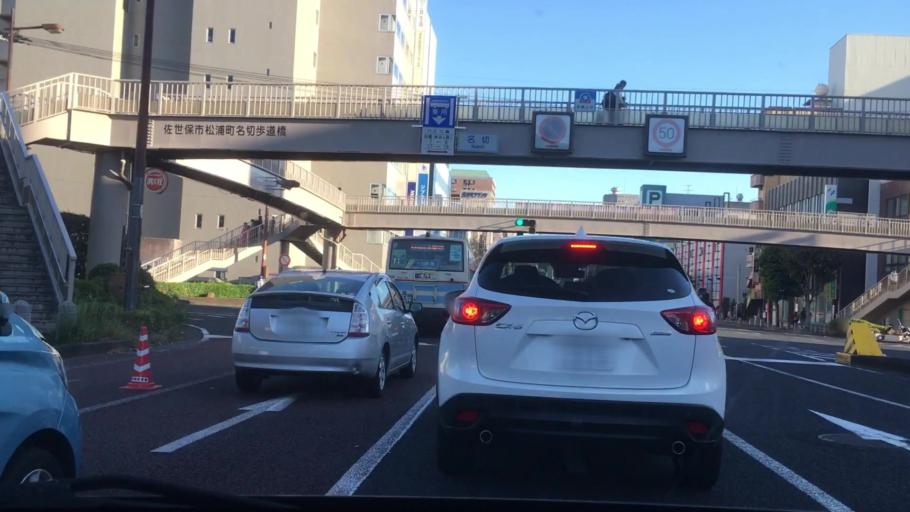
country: JP
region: Nagasaki
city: Sasebo
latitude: 33.1752
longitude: 129.7189
